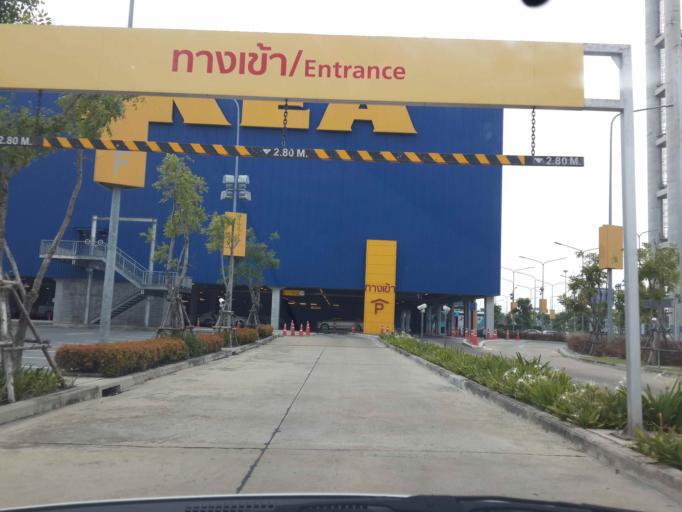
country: TH
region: Bangkok
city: Bang Na
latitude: 13.6433
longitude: 100.6797
